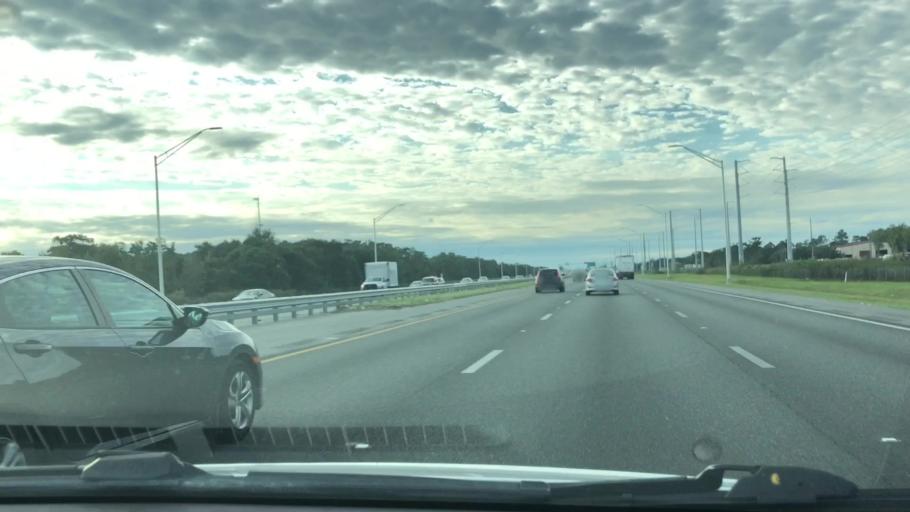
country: US
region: Florida
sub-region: Orange County
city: Union Park
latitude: 28.5346
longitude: -81.2510
